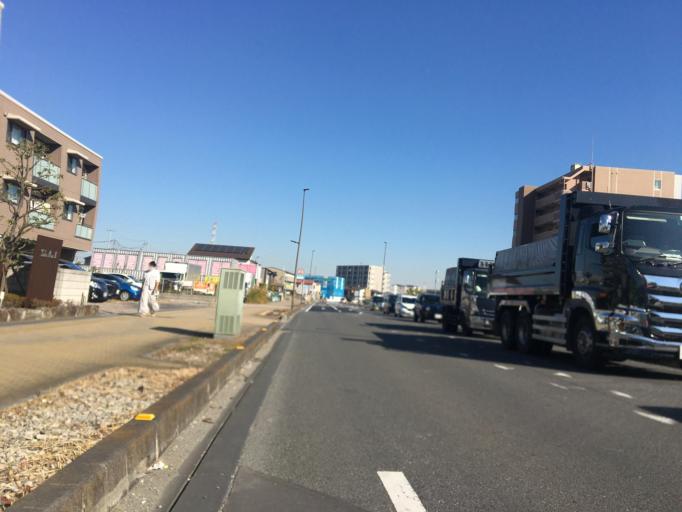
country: JP
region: Saitama
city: Yashio-shi
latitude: 35.8119
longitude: 139.8475
